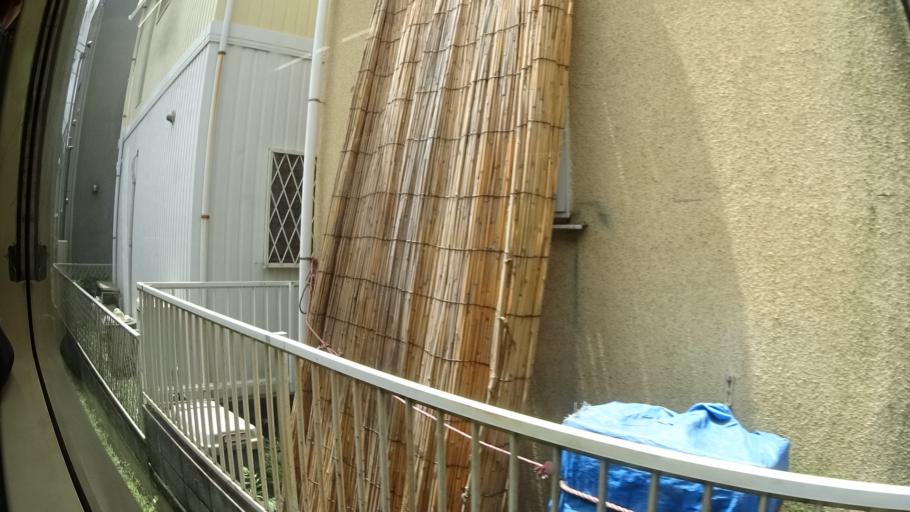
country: JP
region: Kanagawa
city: Fujisawa
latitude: 35.3070
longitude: 139.4949
